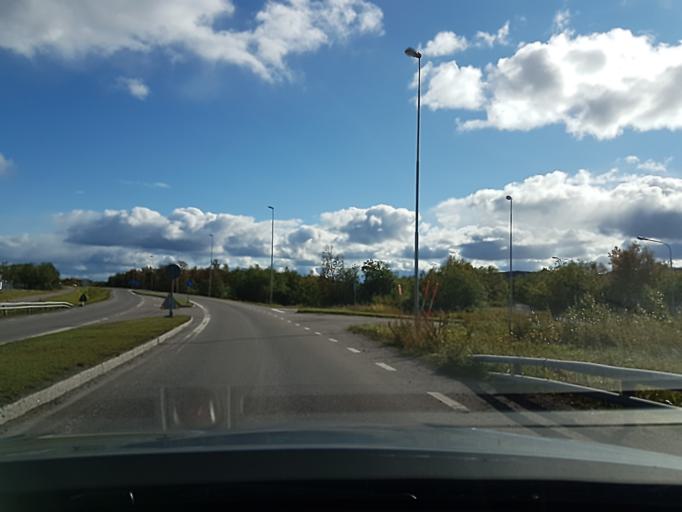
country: SE
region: Norrbotten
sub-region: Kiruna Kommun
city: Kiruna
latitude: 67.8463
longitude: 20.2215
